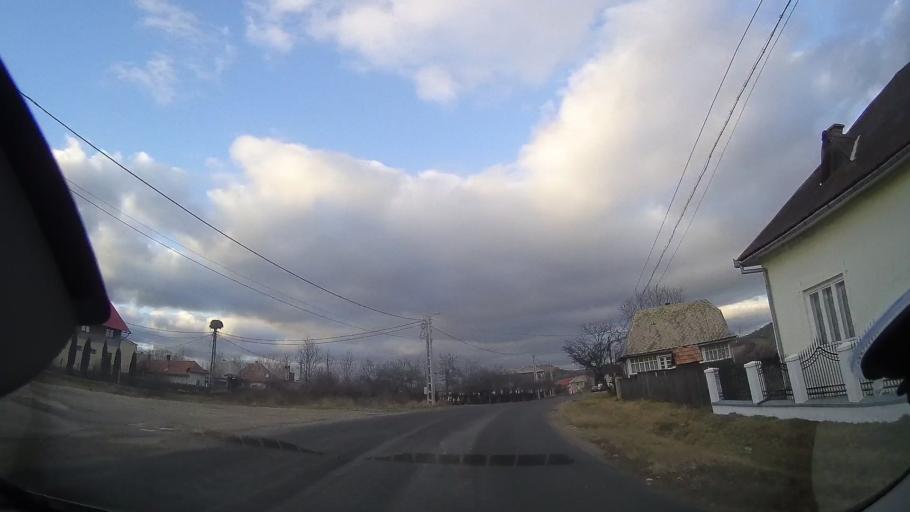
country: RO
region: Cluj
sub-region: Comuna Calatele
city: Calatele
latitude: 46.7748
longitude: 23.0068
